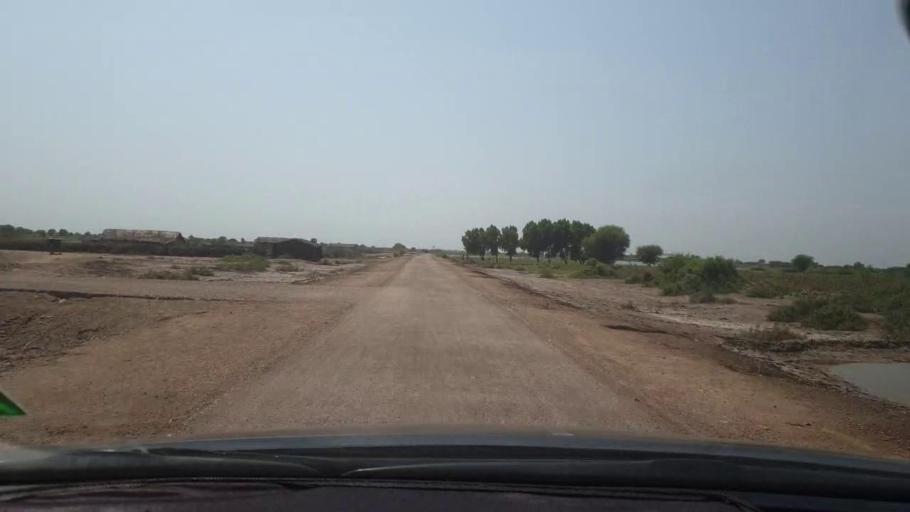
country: PK
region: Sindh
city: Tando Bago
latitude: 24.7984
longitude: 69.1682
